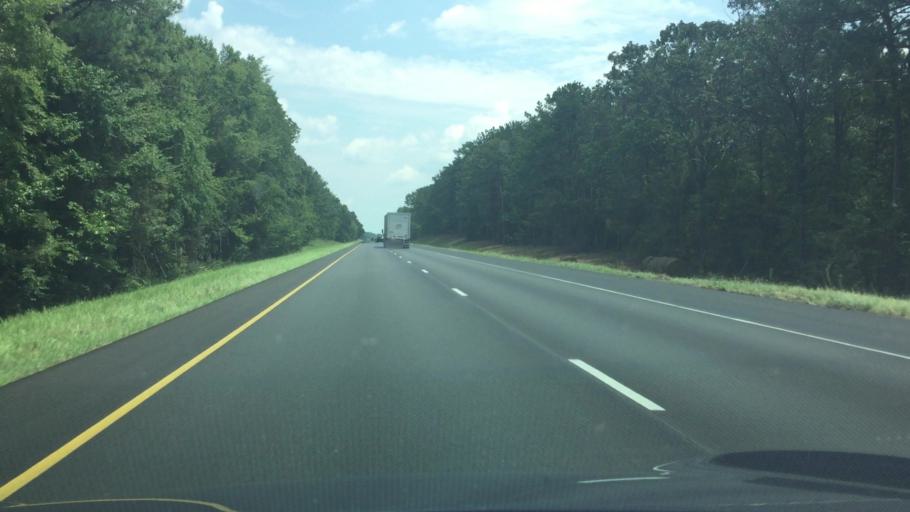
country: US
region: Alabama
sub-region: Saint Clair County
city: Ashville
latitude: 33.8780
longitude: -86.2630
